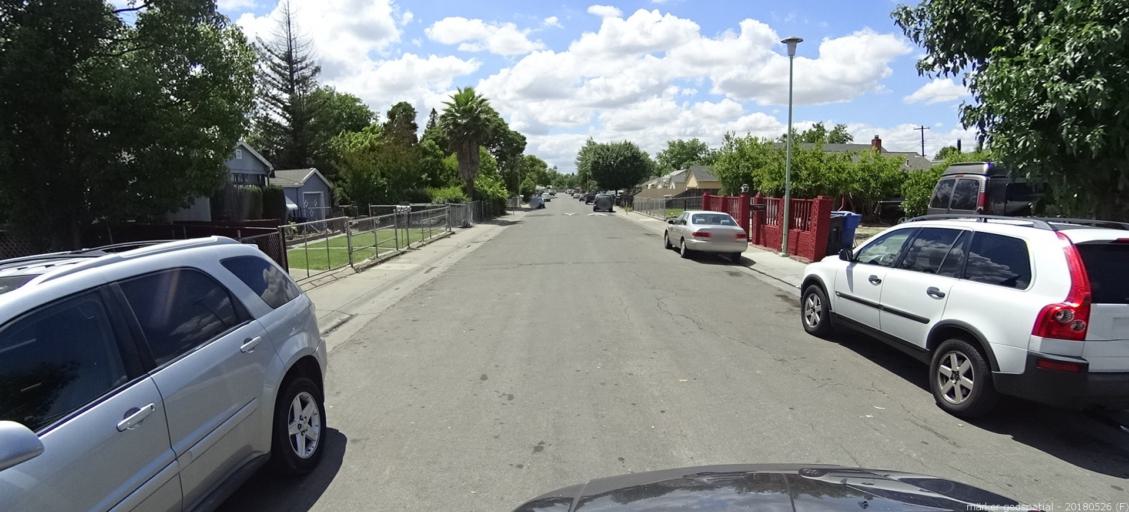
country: US
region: California
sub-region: Sacramento County
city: Sacramento
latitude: 38.6238
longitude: -121.4723
